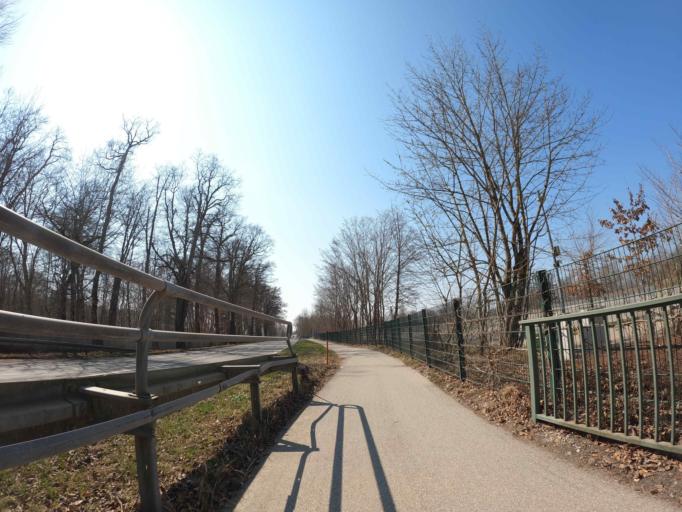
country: DE
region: Bavaria
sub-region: Upper Bavaria
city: Starnberg
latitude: 48.0025
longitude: 11.3811
